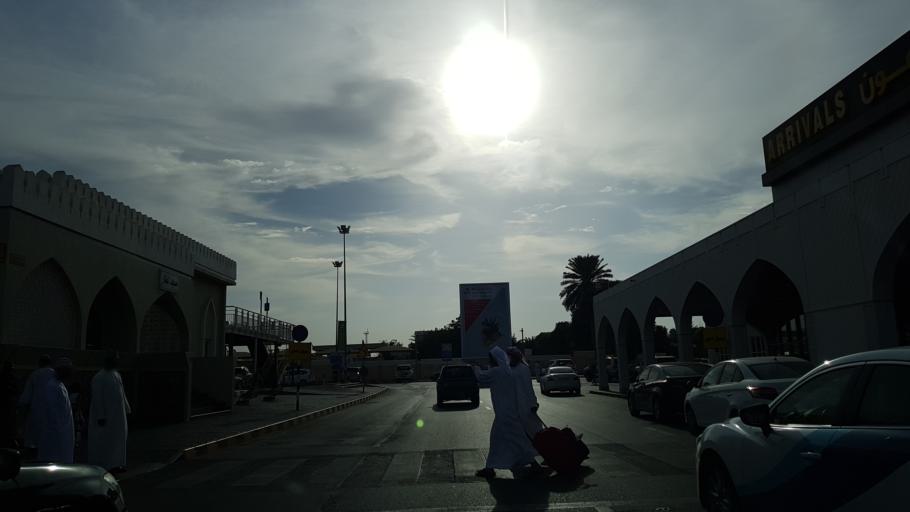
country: OM
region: Muhafazat Masqat
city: Bawshar
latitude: 23.5880
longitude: 58.2898
